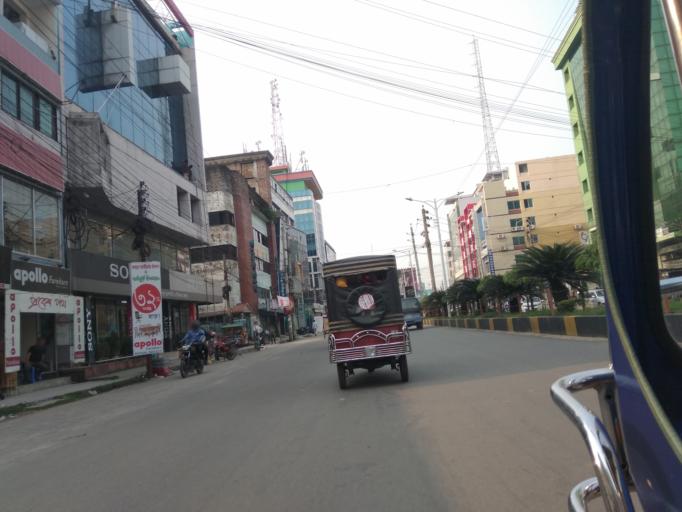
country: BD
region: Khulna
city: Khulna
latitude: 22.8194
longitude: 89.5530
